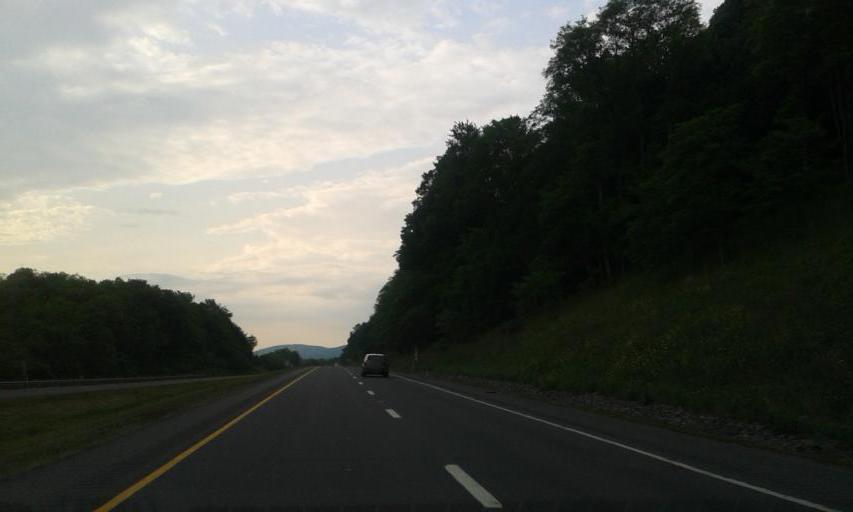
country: US
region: Pennsylvania
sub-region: Susquehanna County
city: Hallstead
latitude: 41.9420
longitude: -75.7343
